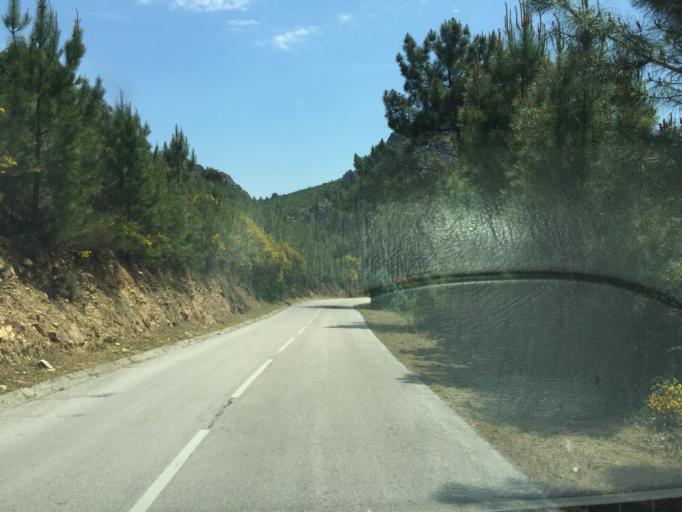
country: PT
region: Coimbra
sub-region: Pampilhosa da Serra
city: Pampilhosa da Serra
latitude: 40.0916
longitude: -7.8667
